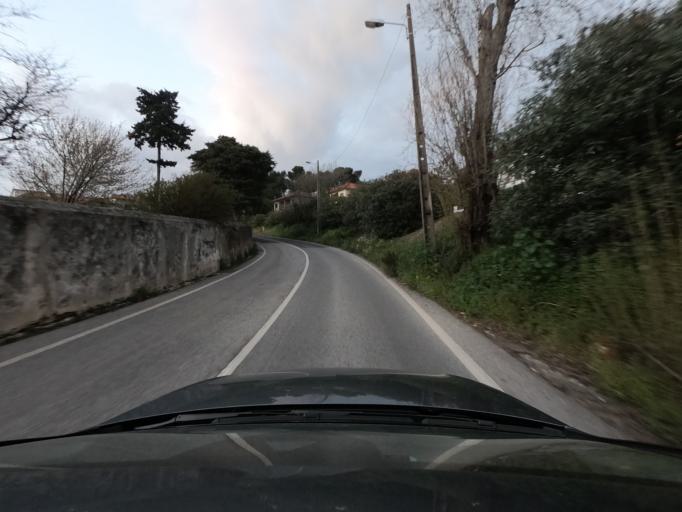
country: PT
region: Lisbon
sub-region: Oeiras
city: Terrugem
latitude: 38.7011
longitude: -9.2724
